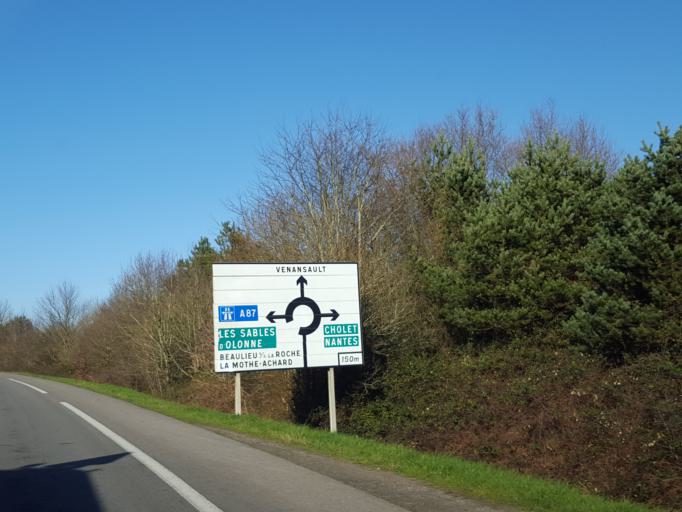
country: FR
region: Pays de la Loire
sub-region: Departement de la Vendee
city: La Roche-sur-Yon
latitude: 46.6634
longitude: -1.4628
